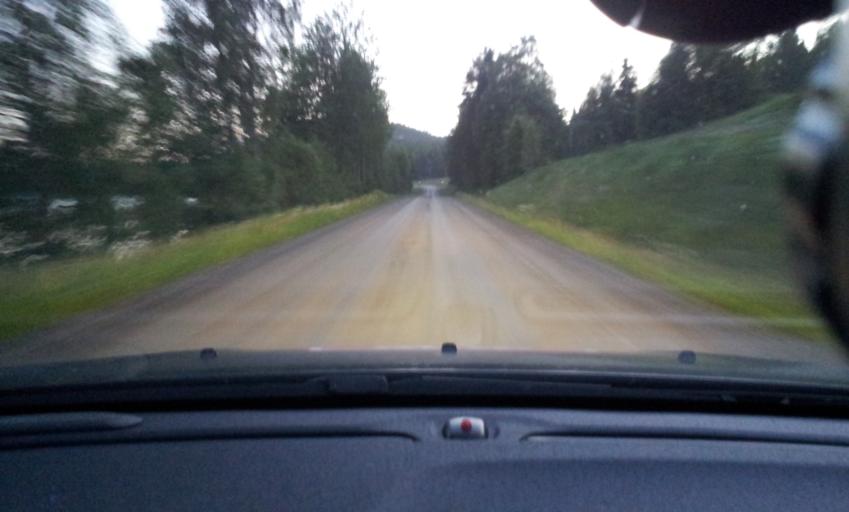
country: SE
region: Jaemtland
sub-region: Braecke Kommun
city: Braecke
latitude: 62.7181
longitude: 15.5897
